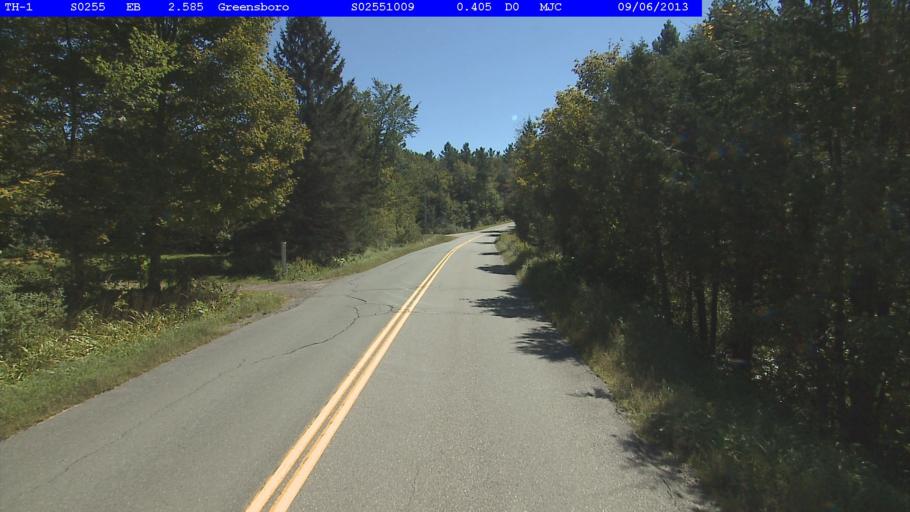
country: US
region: Vermont
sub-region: Caledonia County
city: Hardwick
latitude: 44.6345
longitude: -72.3289
